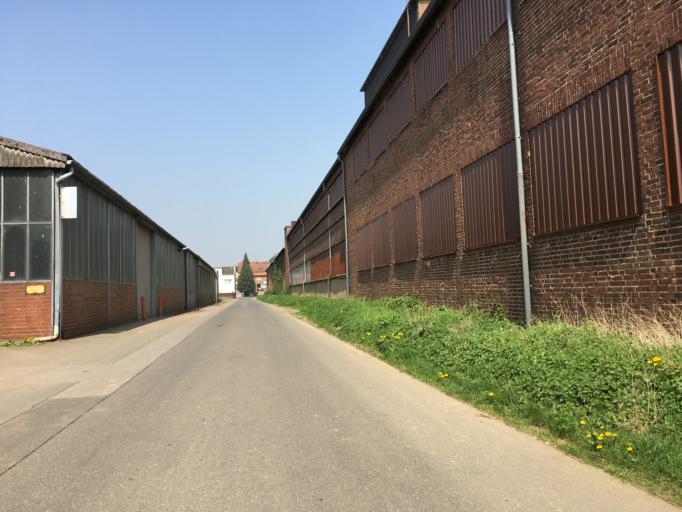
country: DE
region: North Rhine-Westphalia
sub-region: Regierungsbezirk Koln
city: Dueren
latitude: 50.8101
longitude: 6.5127
